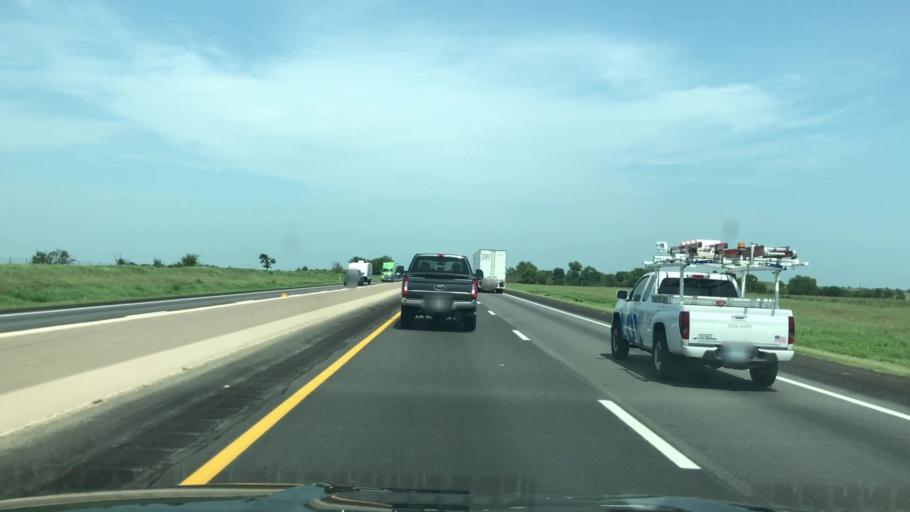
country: US
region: Oklahoma
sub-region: Ottawa County
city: Afton
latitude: 36.6812
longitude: -95.0410
